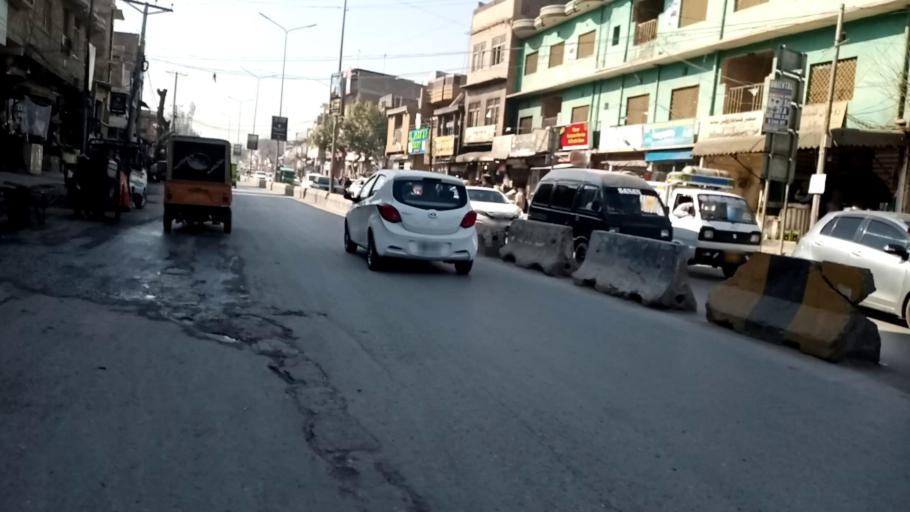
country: PK
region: Khyber Pakhtunkhwa
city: Peshawar
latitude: 33.9826
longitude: 71.5248
